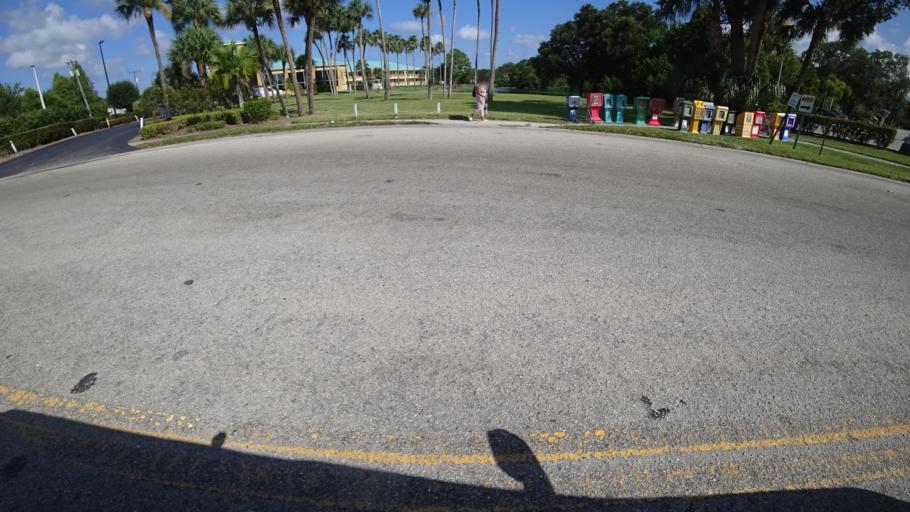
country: US
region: Florida
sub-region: Manatee County
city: Ellenton
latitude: 27.4932
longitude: -82.4786
